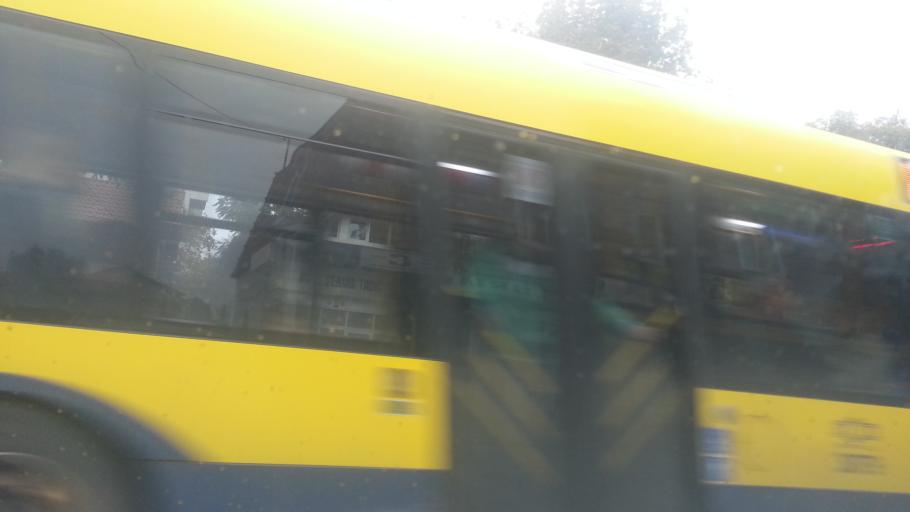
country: RS
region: Central Serbia
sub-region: Belgrade
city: Zemun
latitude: 44.8415
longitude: 20.3889
